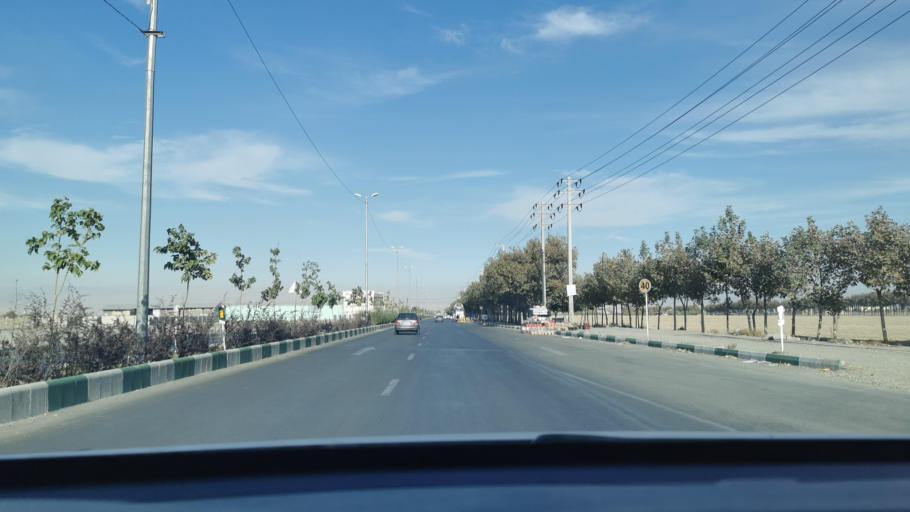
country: IR
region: Razavi Khorasan
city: Torqabeh
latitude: 36.4325
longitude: 59.4265
